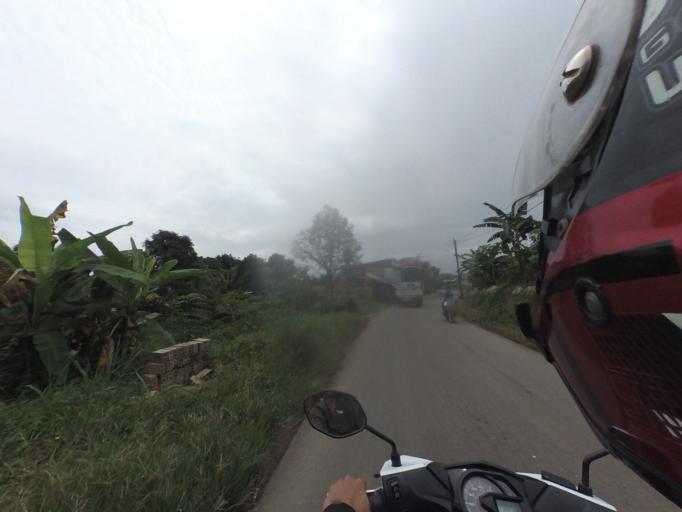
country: ID
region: West Java
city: Bogor
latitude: -6.6366
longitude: 106.7478
